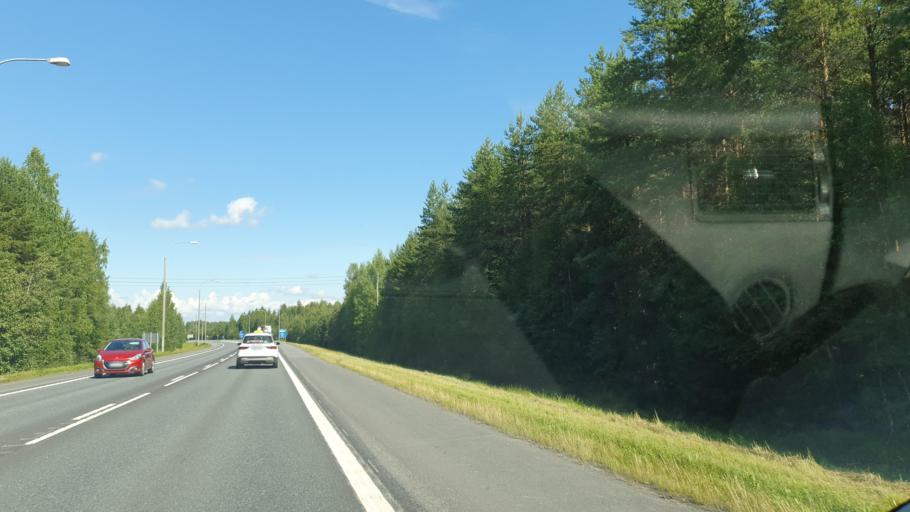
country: FI
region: Northern Savo
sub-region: Ylae-Savo
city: Iisalmi
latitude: 63.5131
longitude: 27.2570
